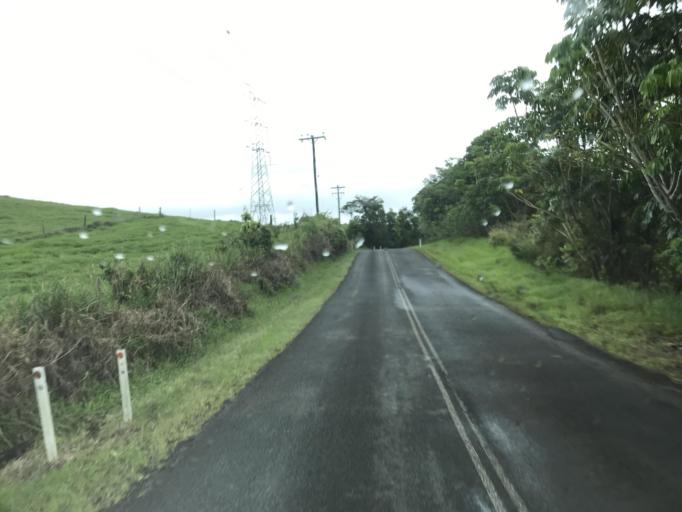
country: AU
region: Queensland
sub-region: Cassowary Coast
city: Innisfail
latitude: -17.5168
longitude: 145.9736
